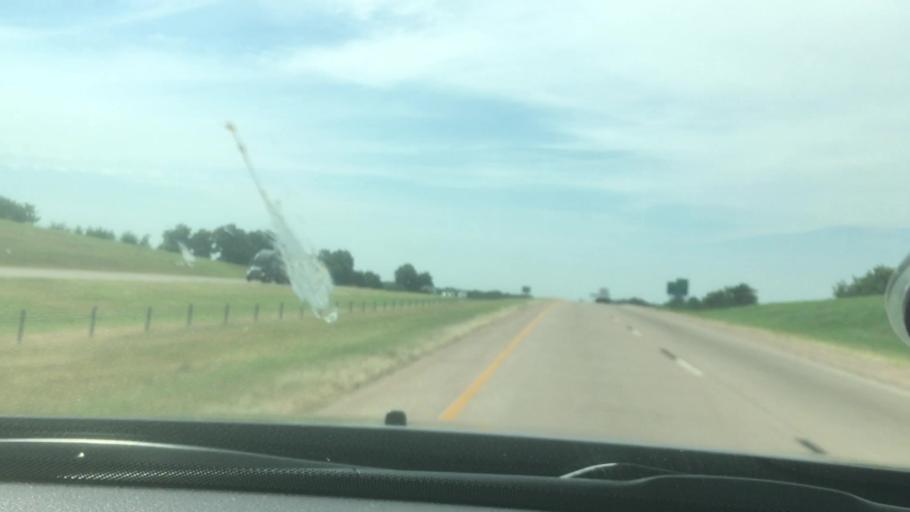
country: US
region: Oklahoma
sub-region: Garvin County
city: Pauls Valley
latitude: 34.7247
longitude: -97.2541
